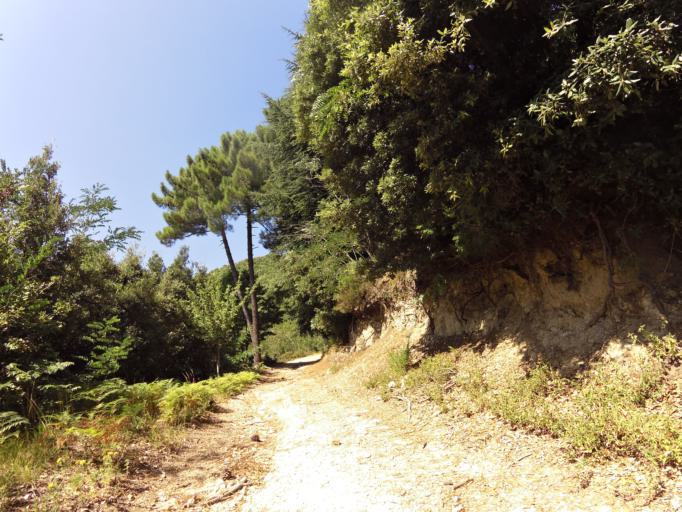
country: IT
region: Calabria
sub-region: Provincia di Reggio Calabria
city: Bivongi
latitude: 38.5108
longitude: 16.4296
